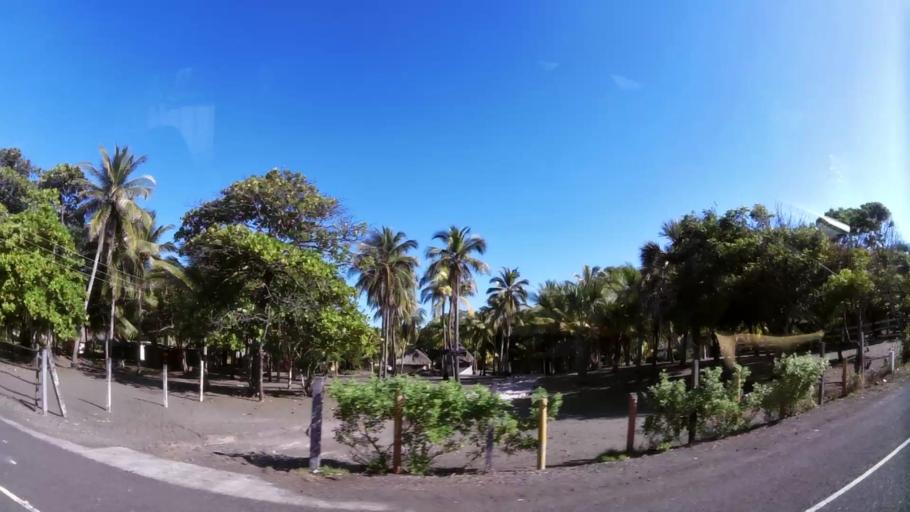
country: GT
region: Santa Rosa
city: Guazacapan
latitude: 13.8650
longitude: -90.4101
